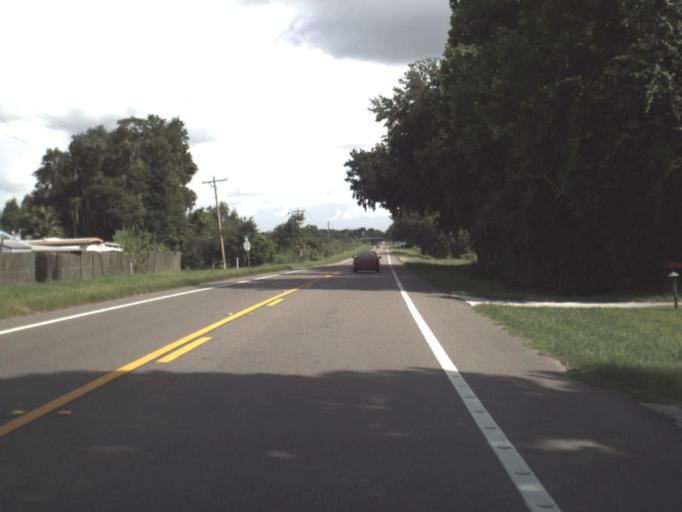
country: US
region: Florida
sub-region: Pasco County
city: Crystal Springs
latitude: 28.2003
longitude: -82.1707
